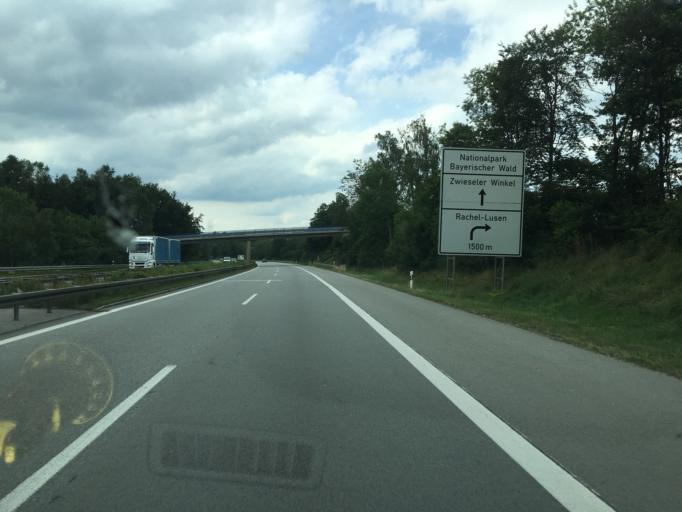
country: DE
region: Bavaria
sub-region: Lower Bavaria
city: Aicha vorm Wald
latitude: 48.6501
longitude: 13.2834
